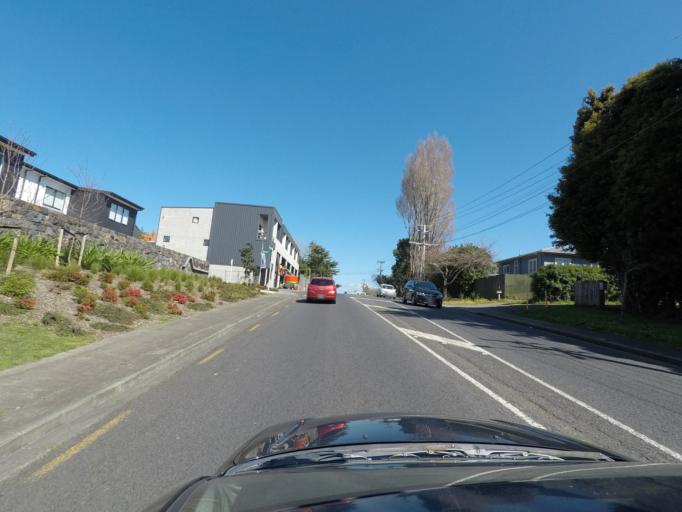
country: NZ
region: Auckland
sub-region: Auckland
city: Tamaki
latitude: -36.9270
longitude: 174.8468
